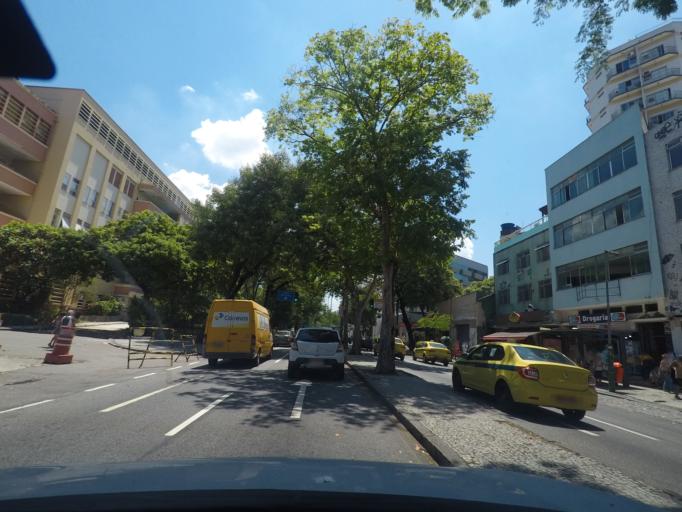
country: BR
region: Rio de Janeiro
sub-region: Rio De Janeiro
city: Rio de Janeiro
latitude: -22.9140
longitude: -43.2367
